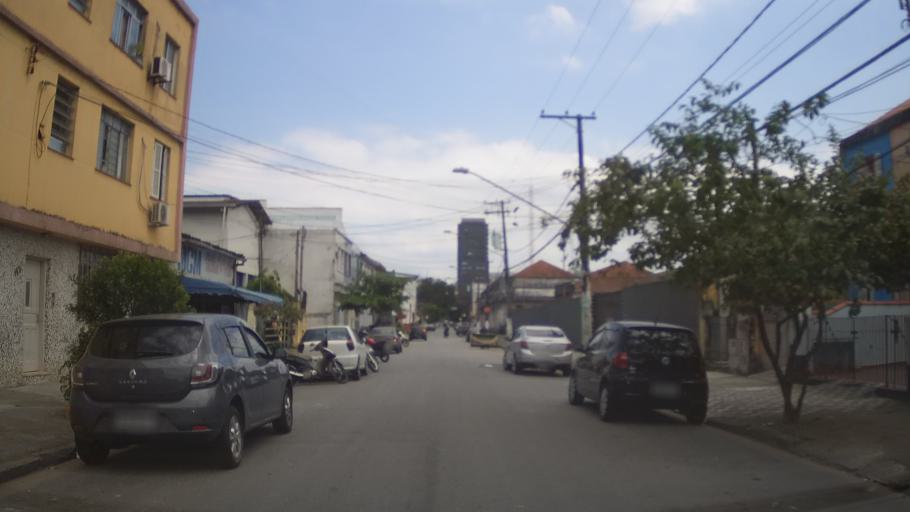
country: BR
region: Sao Paulo
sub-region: Santos
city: Santos
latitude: -23.9537
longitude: -46.3174
